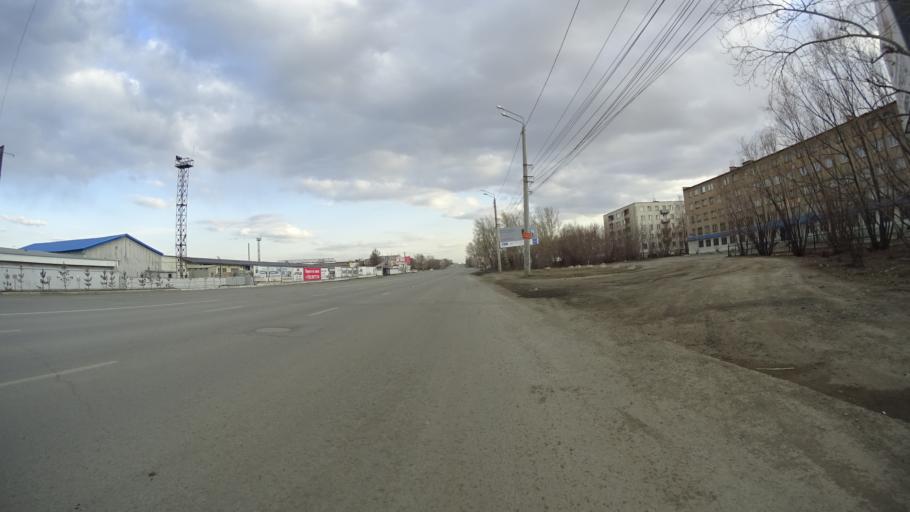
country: RU
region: Chelyabinsk
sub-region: Gorod Chelyabinsk
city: Chelyabinsk
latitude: 55.1085
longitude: 61.3869
